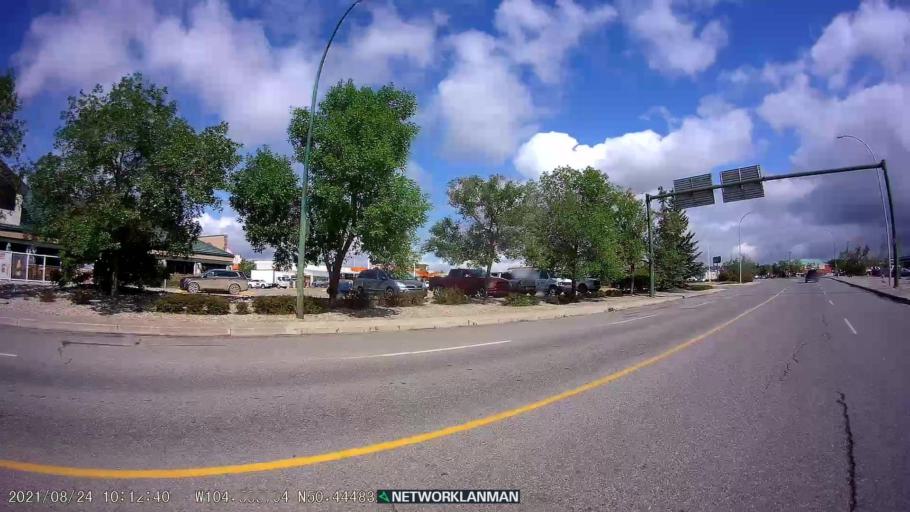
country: CA
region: Saskatchewan
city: Regina
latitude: 50.4447
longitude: -104.5557
